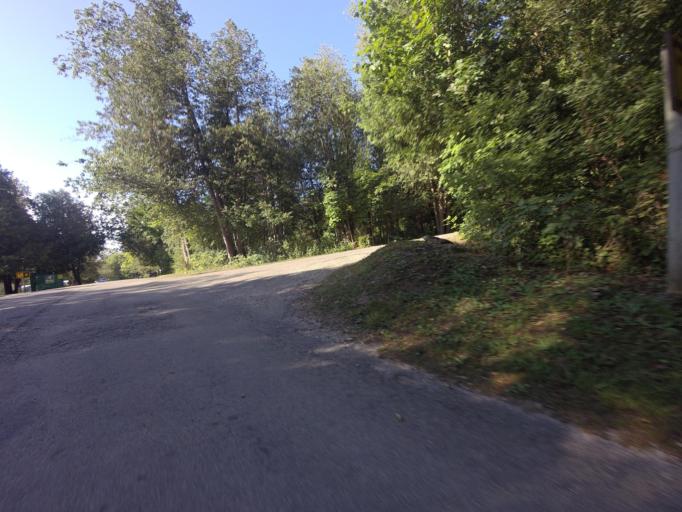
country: CA
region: Ontario
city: Waterloo
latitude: 43.6652
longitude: -80.4499
